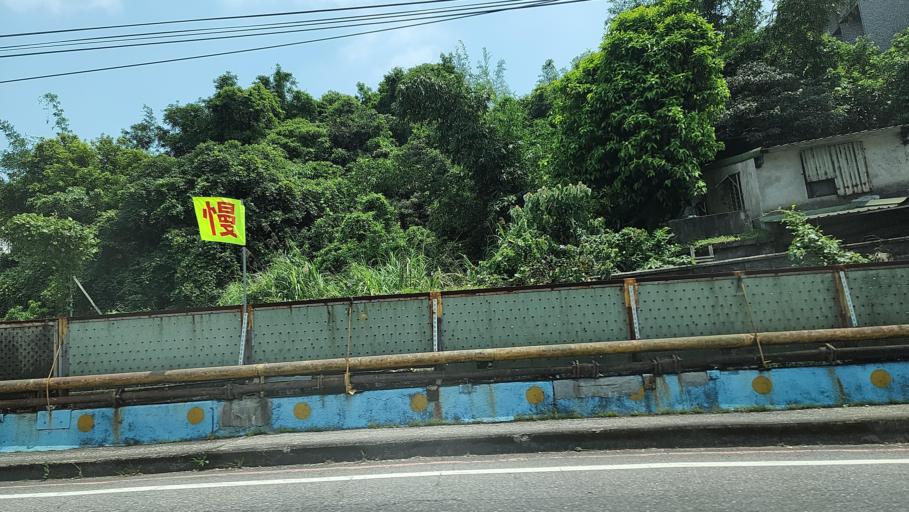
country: TW
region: Taiwan
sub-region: Keelung
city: Keelung
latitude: 25.1113
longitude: 121.7351
